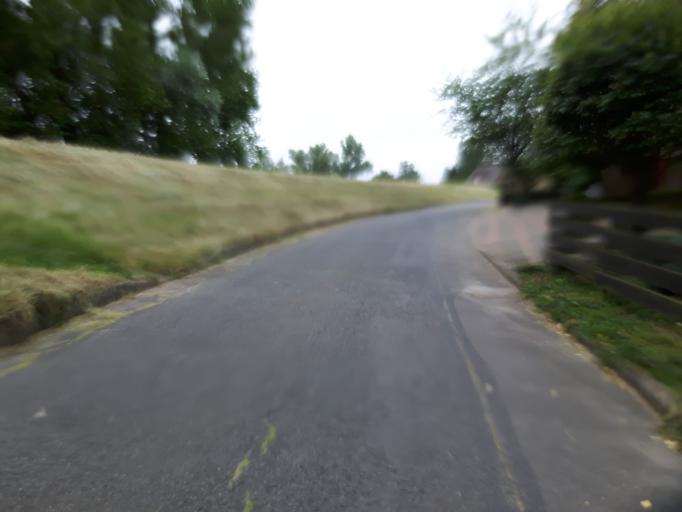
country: DE
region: Lower Saxony
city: Winsen
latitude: 53.3782
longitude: 10.2023
